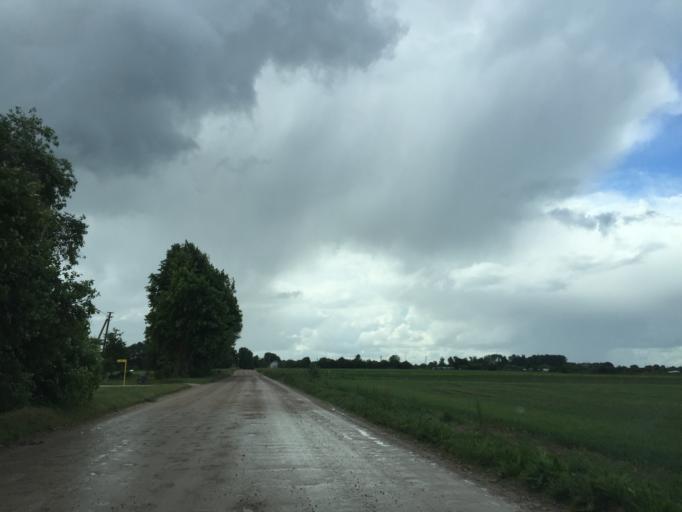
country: LV
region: Lecava
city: Iecava
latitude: 56.6042
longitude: 24.1841
